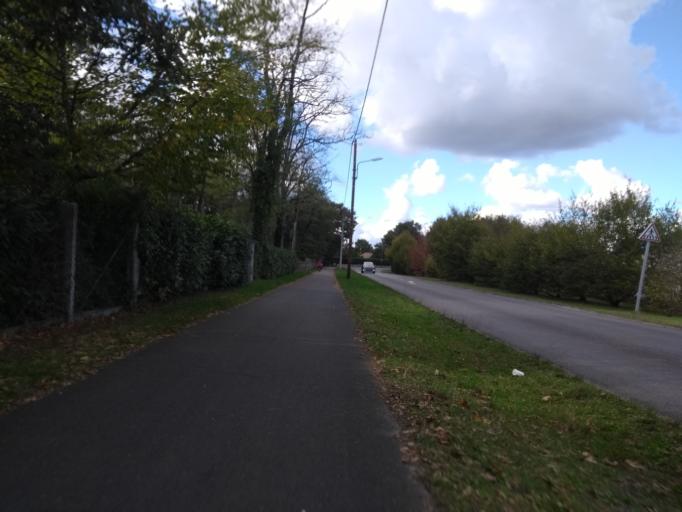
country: FR
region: Aquitaine
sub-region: Departement de la Gironde
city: Cestas
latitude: 44.7371
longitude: -0.6743
